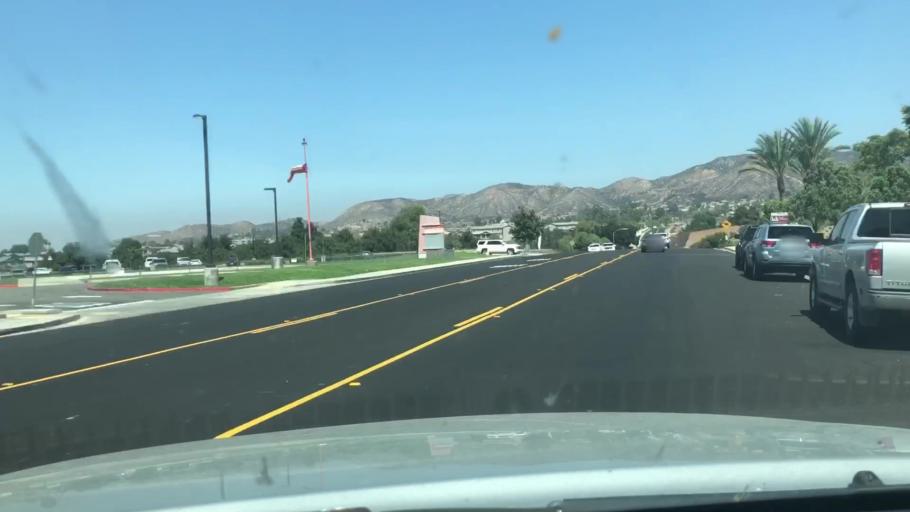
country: US
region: California
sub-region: Riverside County
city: Wildomar
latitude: 33.5920
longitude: -117.2368
